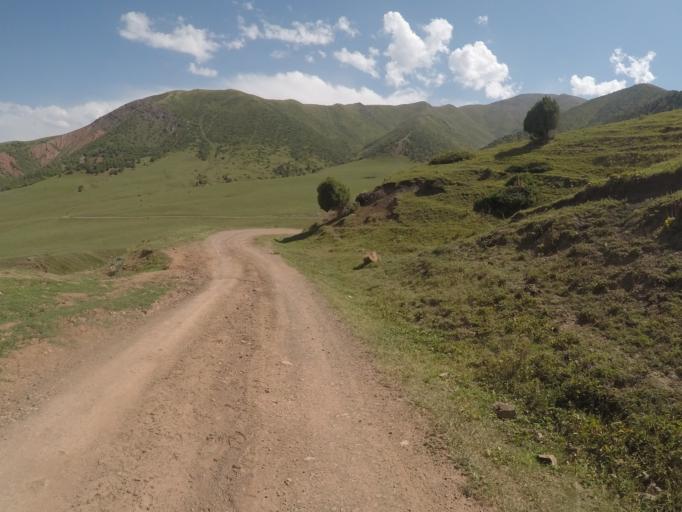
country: KG
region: Chuy
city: Bishkek
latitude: 42.6456
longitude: 74.5696
